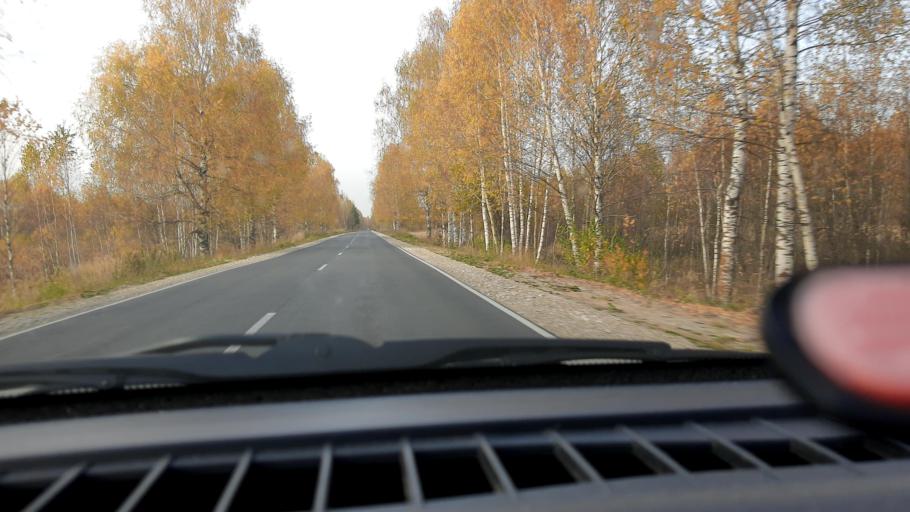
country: RU
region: Nizjnij Novgorod
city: Neklyudovo
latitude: 56.4933
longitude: 43.8582
